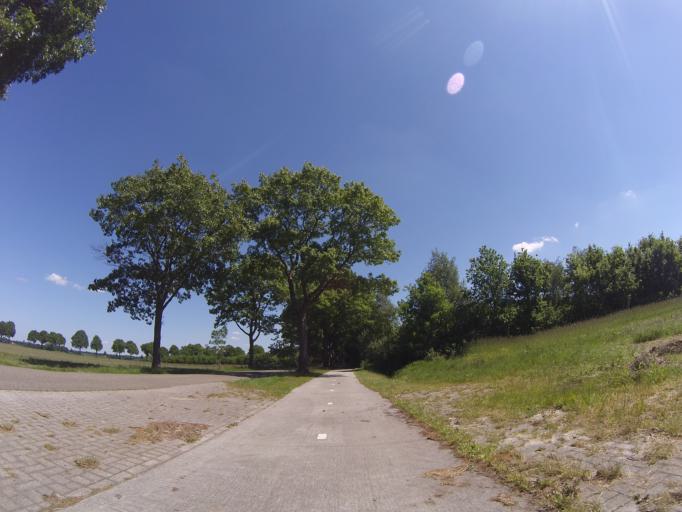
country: NL
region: Drenthe
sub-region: Gemeente Coevorden
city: Dalen
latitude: 52.7966
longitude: 6.6241
